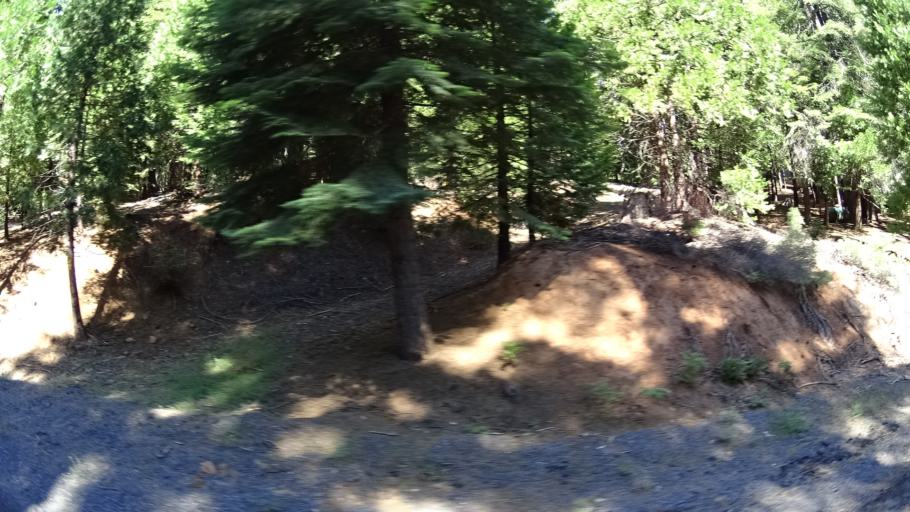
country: US
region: California
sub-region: Calaveras County
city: Arnold
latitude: 38.2978
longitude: -120.2673
